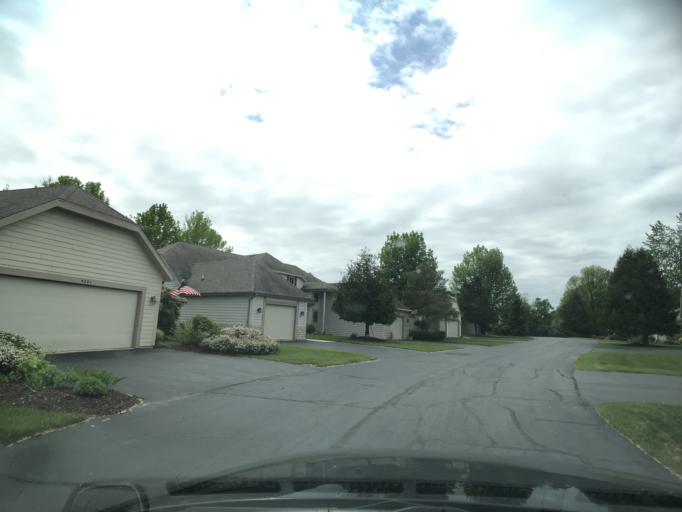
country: US
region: Wisconsin
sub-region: Door County
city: Sturgeon Bay
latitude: 45.1777
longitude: -87.1513
